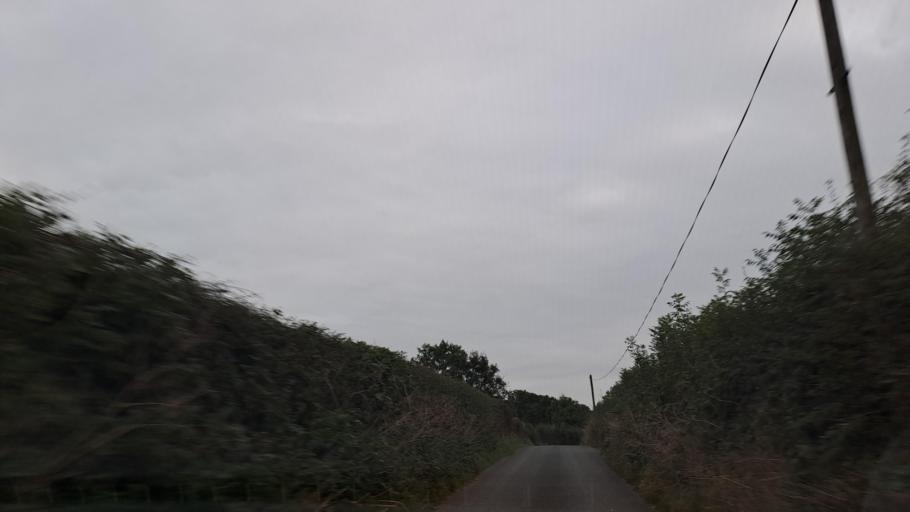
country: IE
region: Ulster
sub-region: County Monaghan
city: Carrickmacross
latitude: 54.0316
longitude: -6.8150
